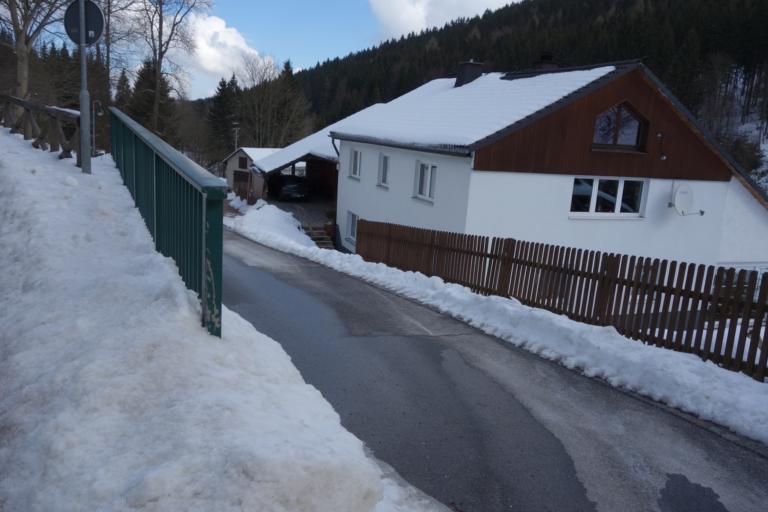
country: DE
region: Saxony
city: Sosa
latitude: 50.4560
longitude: 12.6322
